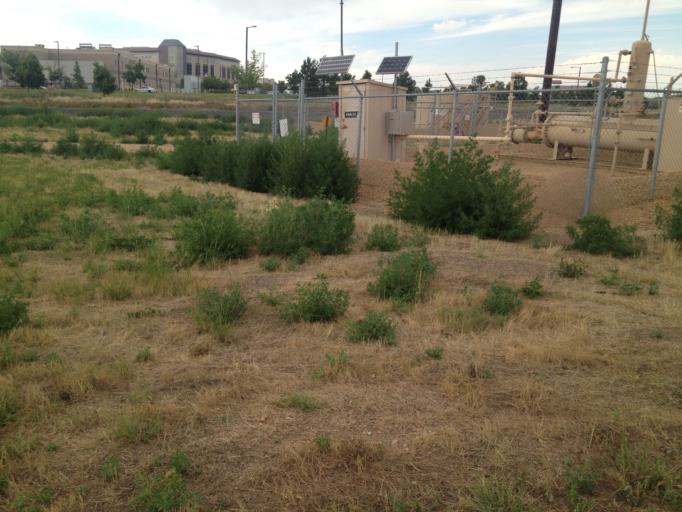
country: US
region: Colorado
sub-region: Boulder County
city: Lafayette
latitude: 39.9683
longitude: -105.0826
